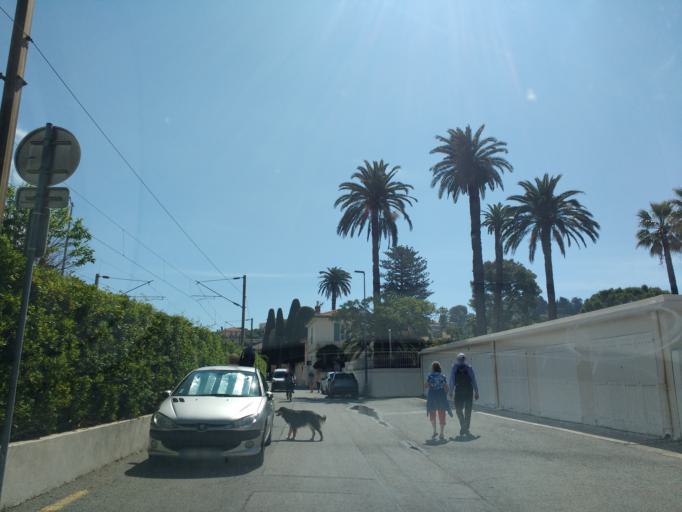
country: FR
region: Provence-Alpes-Cote d'Azur
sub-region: Departement des Alpes-Maritimes
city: Beaulieu-sur-Mer
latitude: 43.7020
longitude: 7.3232
